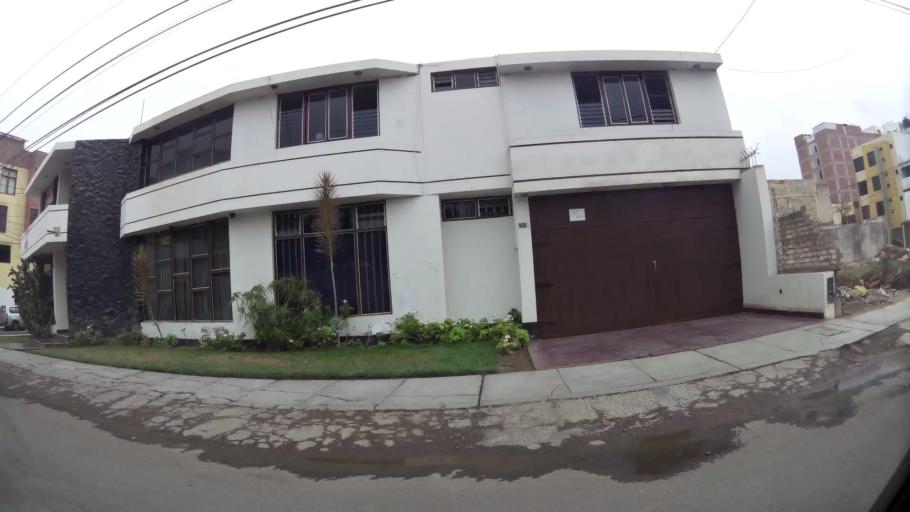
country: PE
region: La Libertad
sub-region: Provincia de Trujillo
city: Buenos Aires
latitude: -8.1334
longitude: -79.0420
